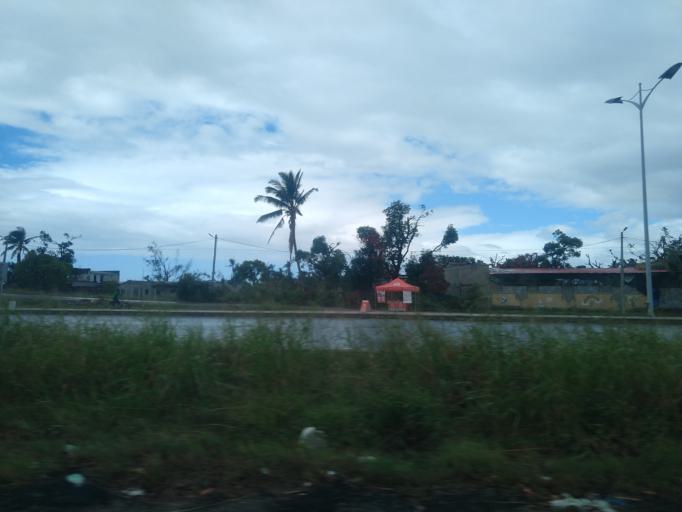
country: MZ
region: Sofala
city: Beira
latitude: -19.7839
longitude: 34.8772
